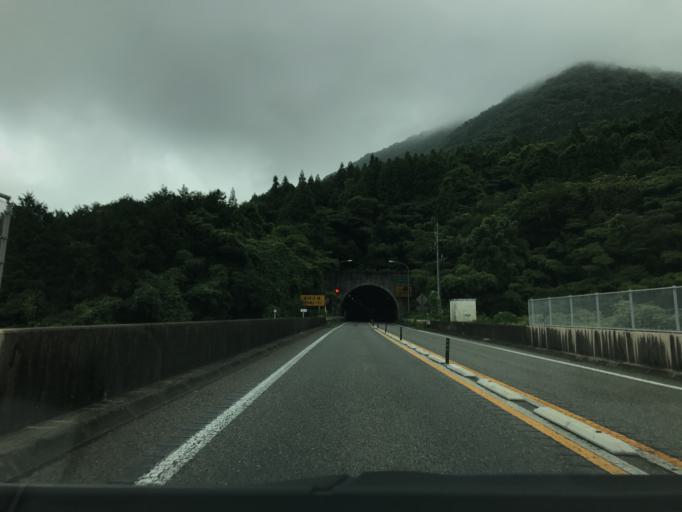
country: JP
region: Oita
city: Bungo-Takada-shi
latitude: 33.4897
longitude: 131.3241
